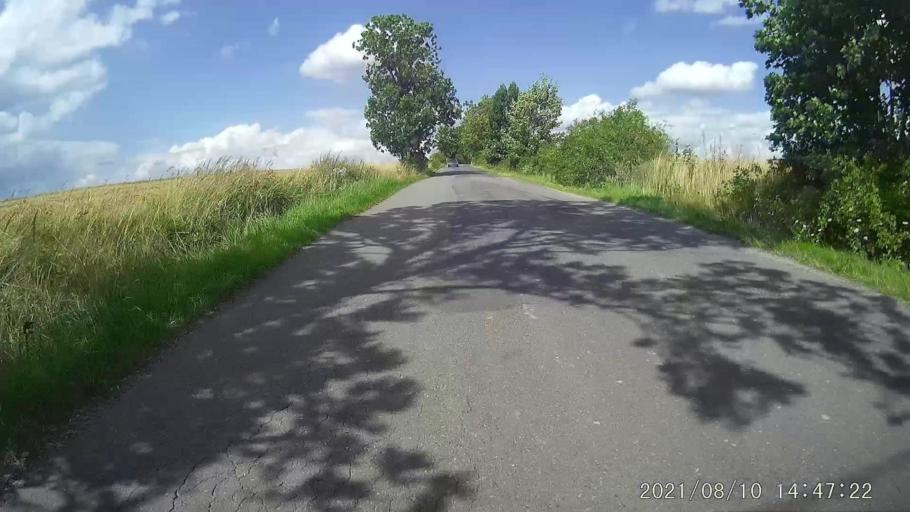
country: PL
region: Lower Silesian Voivodeship
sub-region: Powiat klodzki
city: Radkow
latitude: 50.5228
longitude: 16.4109
